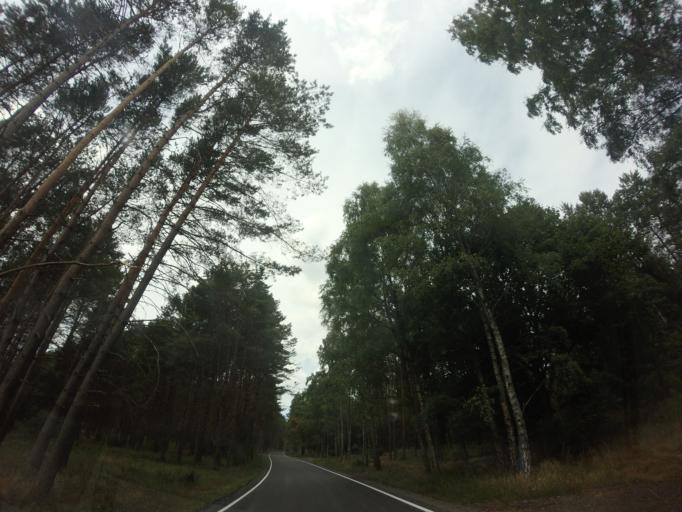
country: PL
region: West Pomeranian Voivodeship
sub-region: Powiat choszczenski
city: Drawno
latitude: 53.1267
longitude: 15.7291
